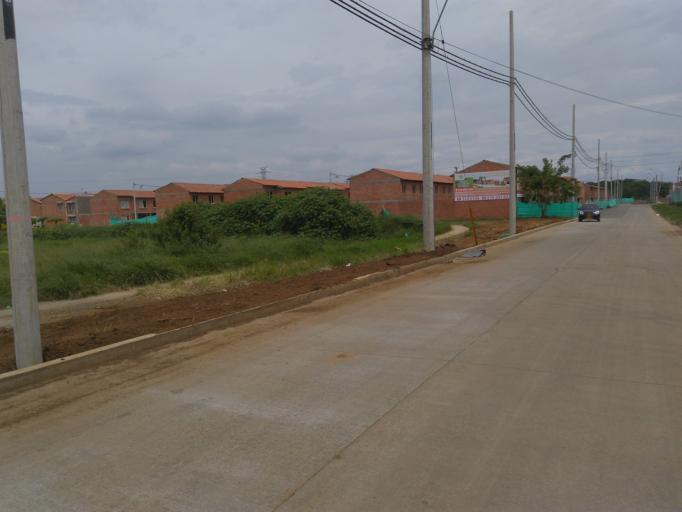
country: CO
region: Valle del Cauca
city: Jamundi
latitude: 3.2565
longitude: -76.5562
